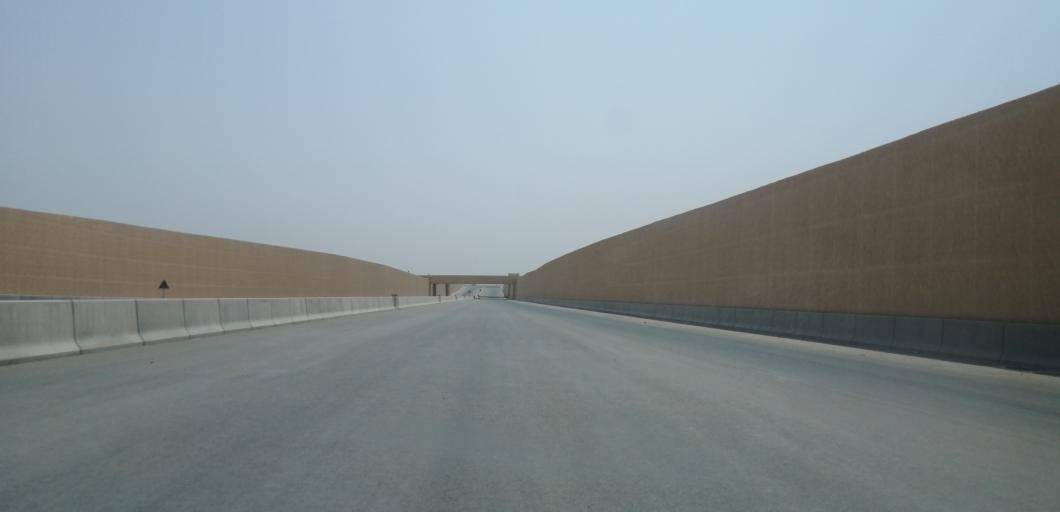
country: KW
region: Muhafazat al Jahra'
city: Al Jahra'
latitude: 29.4537
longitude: 47.5541
